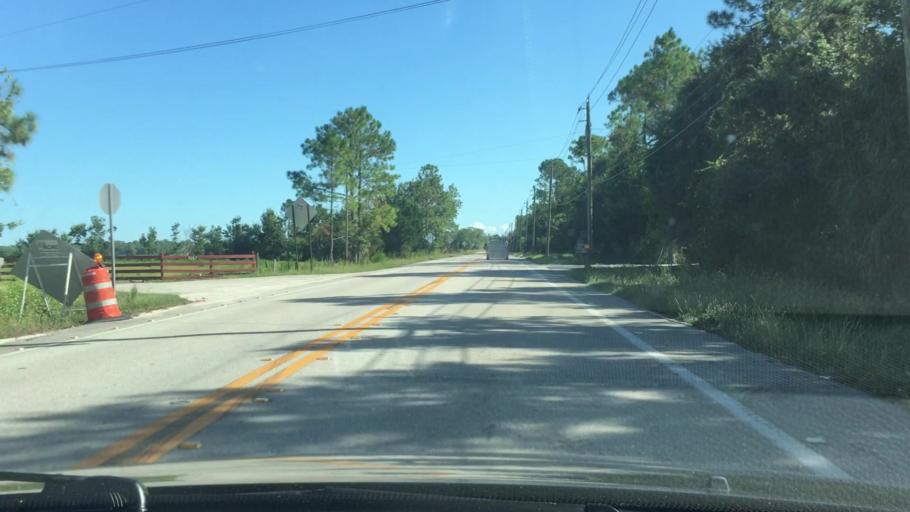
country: US
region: Florida
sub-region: Volusia County
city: South Daytona
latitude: 29.1490
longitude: -81.0816
